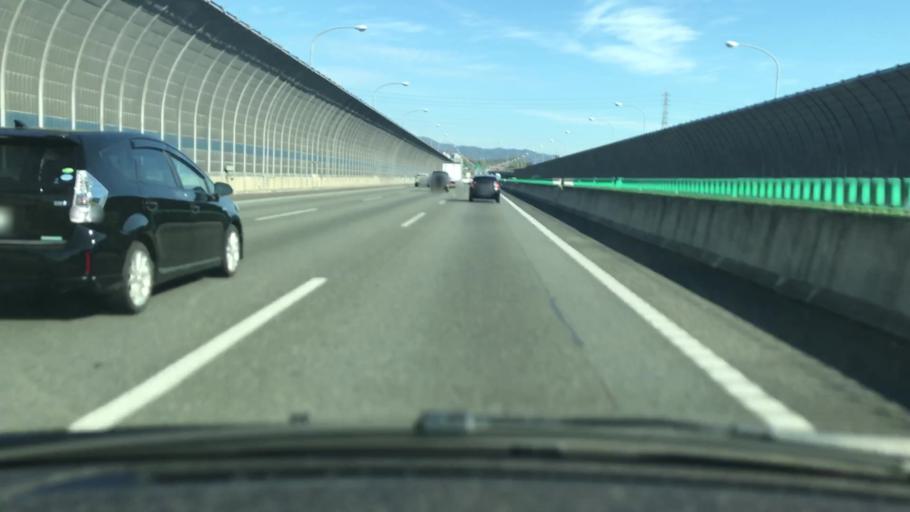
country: JP
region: Osaka
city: Ibaraki
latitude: 34.8384
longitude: 135.5672
